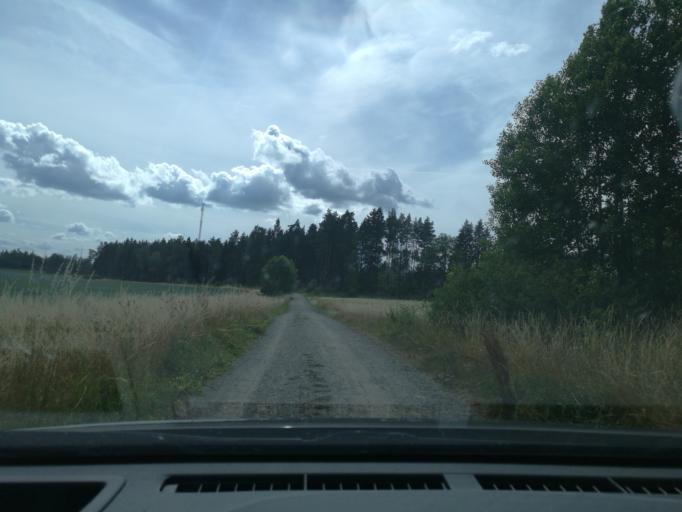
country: SE
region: Stockholm
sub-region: Sigtuna Kommun
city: Marsta
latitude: 59.6141
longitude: 17.8002
